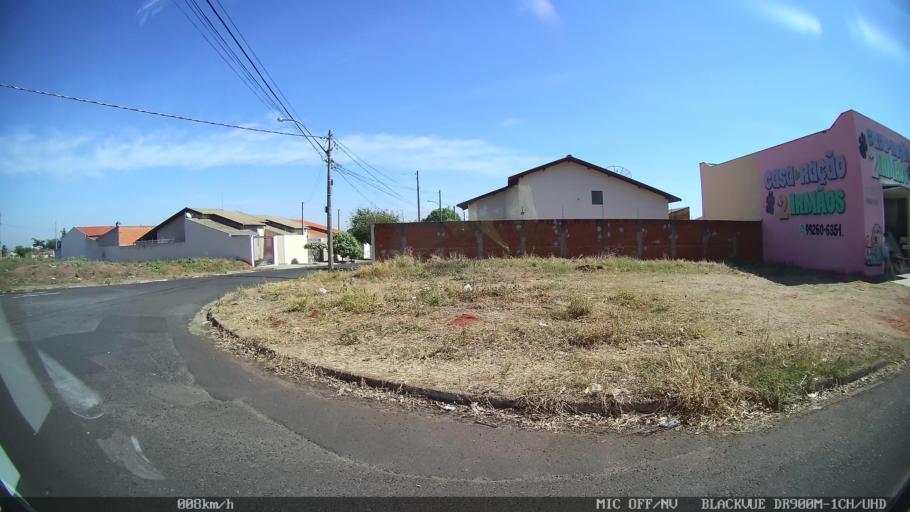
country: BR
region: Sao Paulo
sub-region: Sao Jose Do Rio Preto
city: Sao Jose do Rio Preto
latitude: -20.7681
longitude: -49.4128
